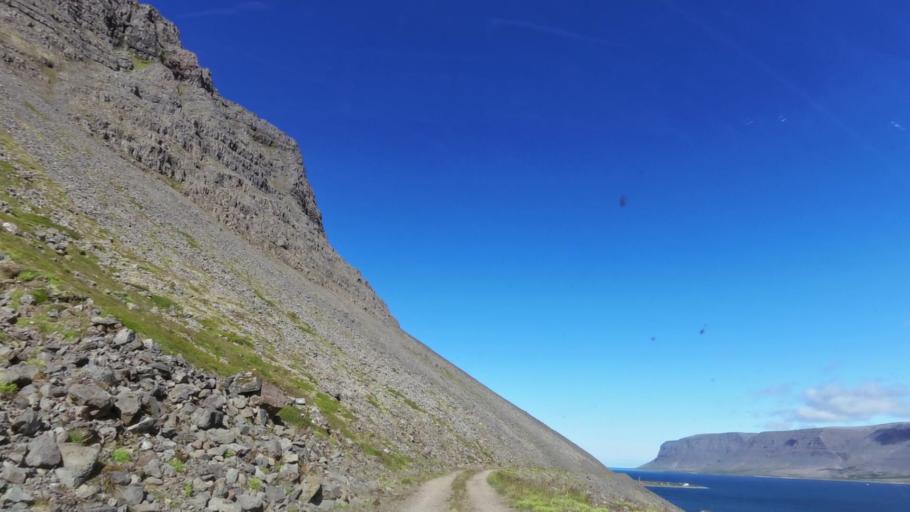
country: IS
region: West
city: Olafsvik
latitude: 65.6299
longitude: -23.9116
